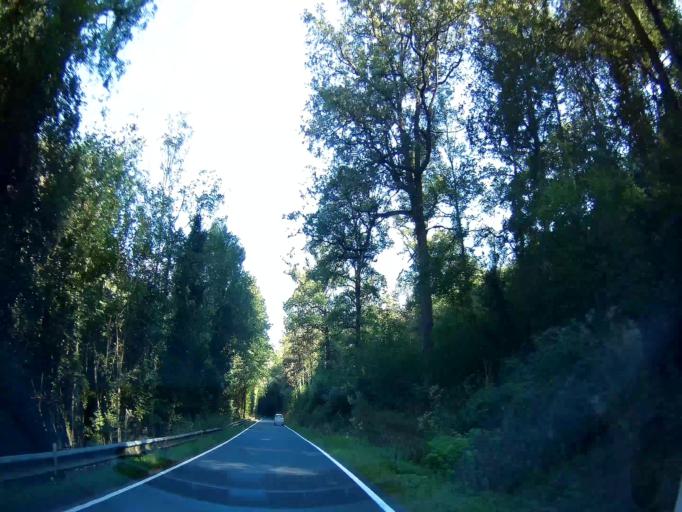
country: BE
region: Wallonia
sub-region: Province de Namur
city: Mettet
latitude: 50.3108
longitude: 4.7621
